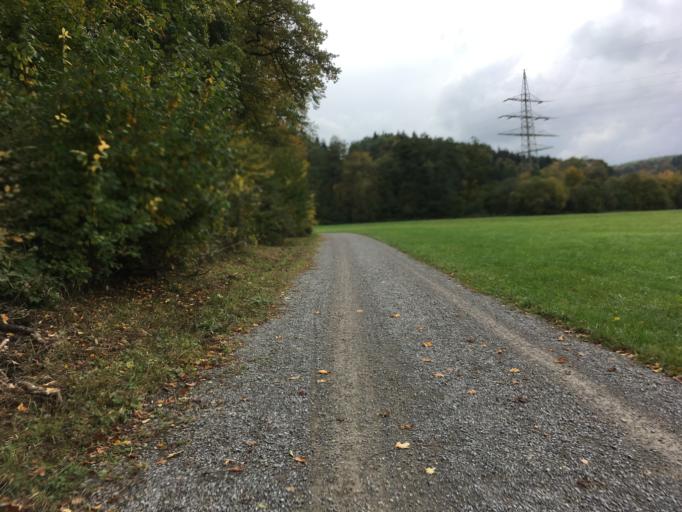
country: DE
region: Baden-Wuerttemberg
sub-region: Tuebingen Region
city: Dusslingen
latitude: 48.4849
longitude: 9.0702
